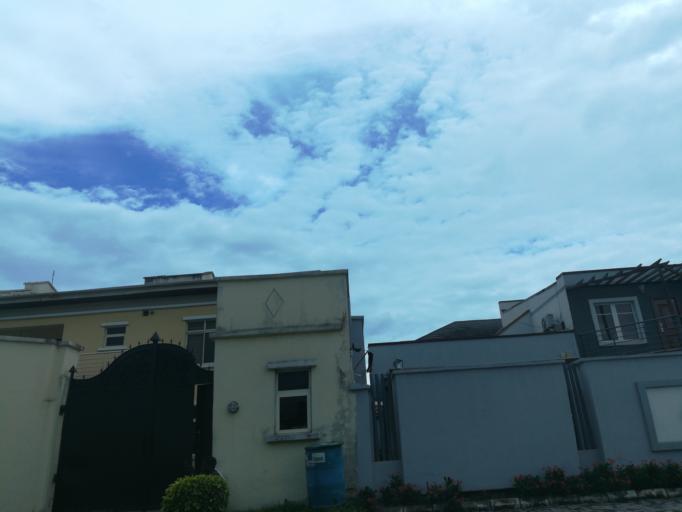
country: NG
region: Lagos
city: Ikoyi
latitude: 6.4418
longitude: 3.4781
